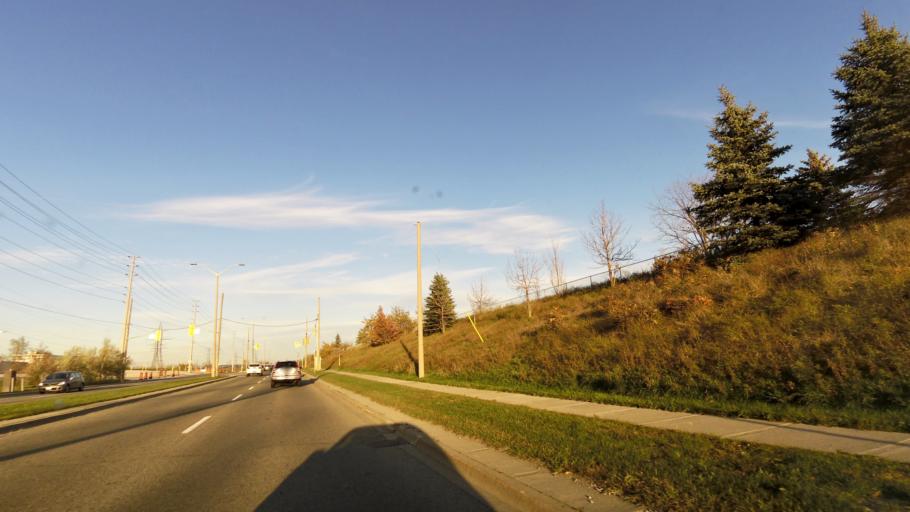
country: CA
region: Ontario
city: Etobicoke
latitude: 43.6316
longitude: -79.6120
